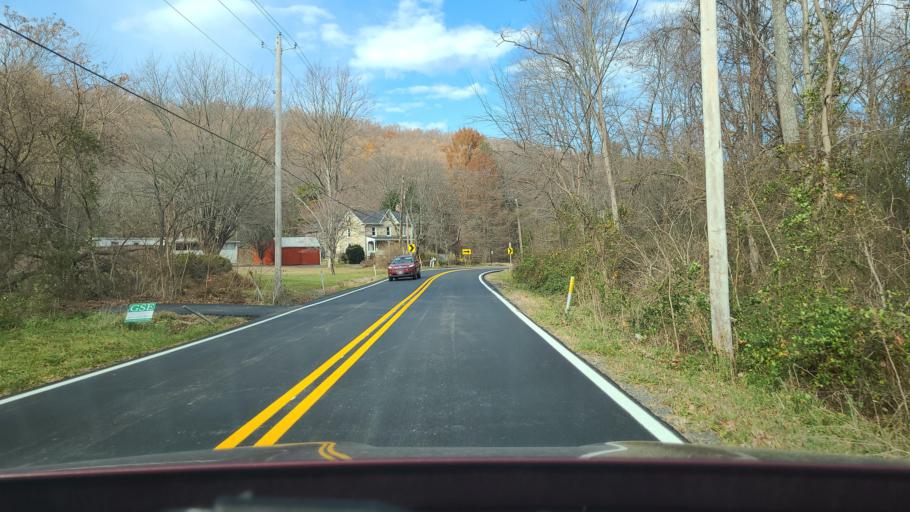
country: US
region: Maryland
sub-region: Frederick County
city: Brunswick
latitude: 39.3819
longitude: -77.6412
